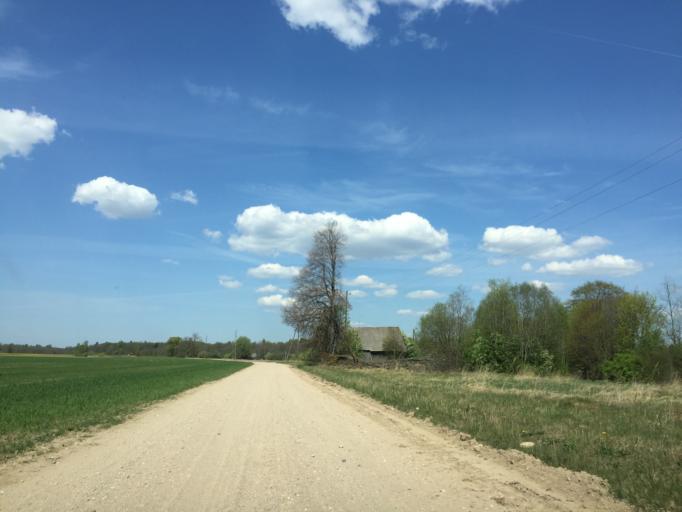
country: LV
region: Limbazu Rajons
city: Limbazi
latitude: 57.3724
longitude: 24.6327
